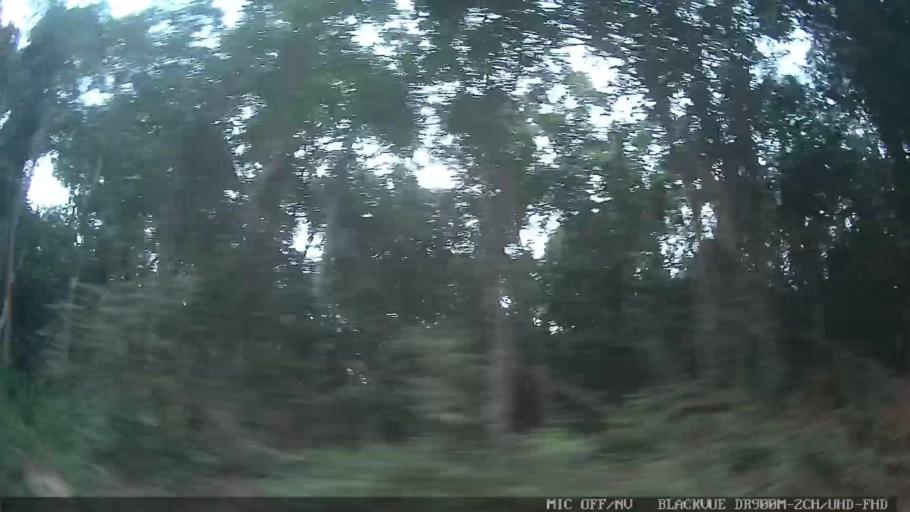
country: BR
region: Sao Paulo
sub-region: Suzano
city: Suzano
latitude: -23.6750
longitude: -46.2363
